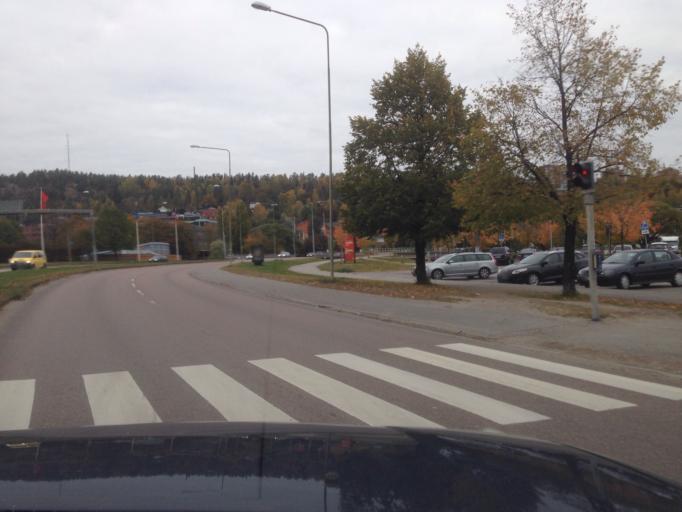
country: SE
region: Vaesternorrland
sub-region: Sundsvalls Kommun
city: Sundsvall
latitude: 62.3917
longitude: 17.3139
